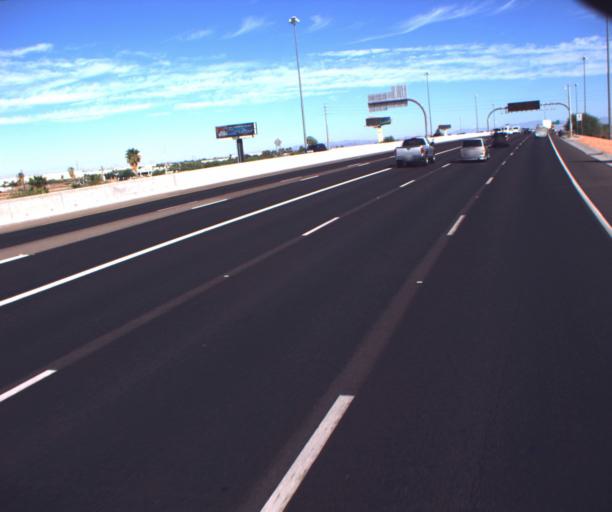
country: US
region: Arizona
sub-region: Maricopa County
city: Peoria
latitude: 33.5342
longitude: -112.2694
